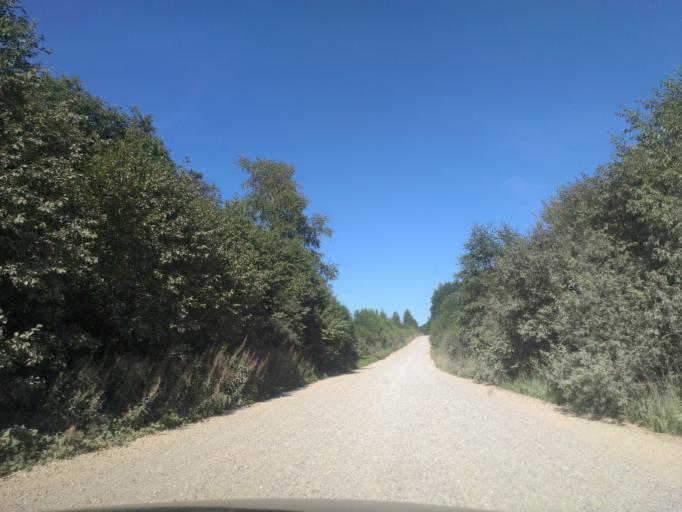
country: LV
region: Amatas Novads
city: Drabesi
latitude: 57.0614
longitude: 25.1738
